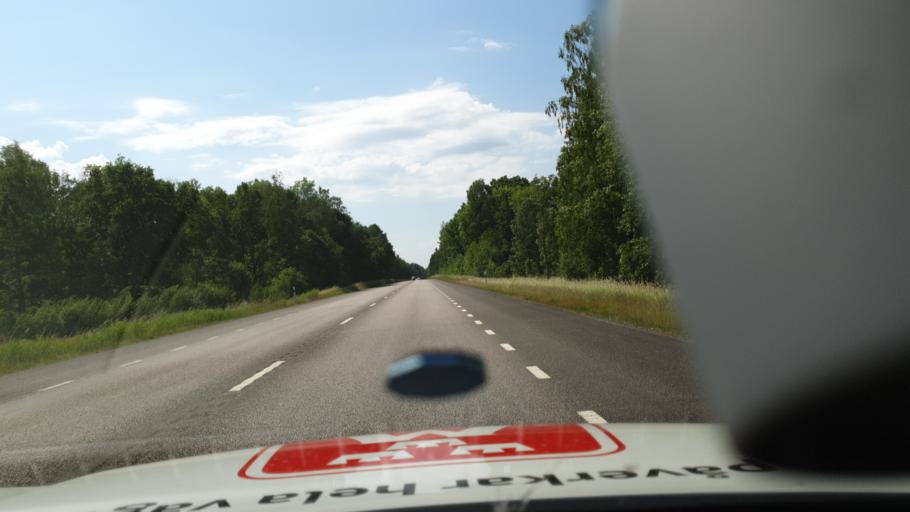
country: SE
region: Vaestra Goetaland
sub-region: Hjo Kommun
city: Hjo
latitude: 58.2798
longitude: 14.2615
